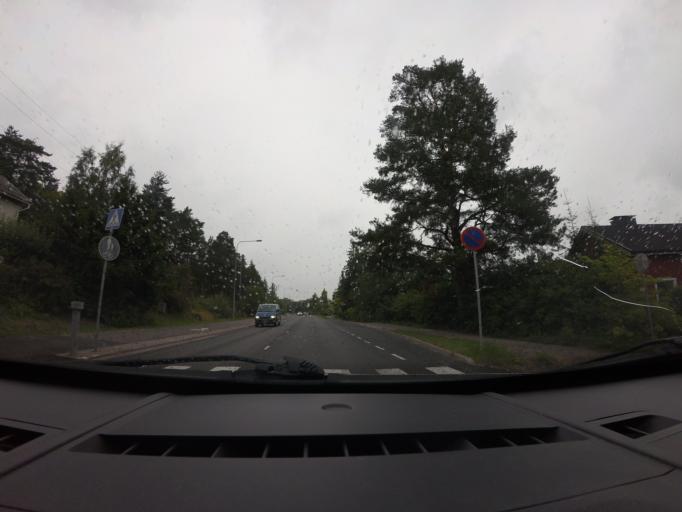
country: FI
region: Varsinais-Suomi
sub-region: Turku
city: Turku
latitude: 60.4249
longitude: 22.2920
